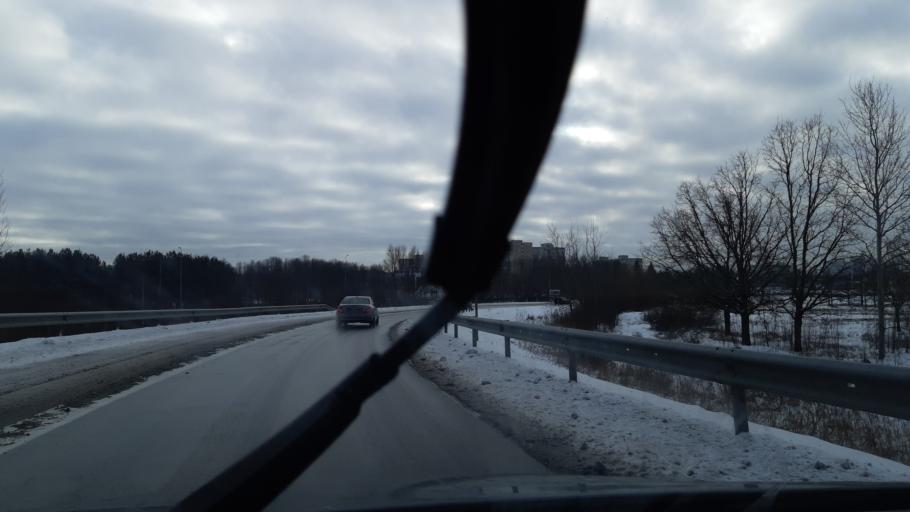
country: LT
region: Kauno apskritis
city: Dainava (Kaunas)
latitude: 54.9329
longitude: 23.9779
